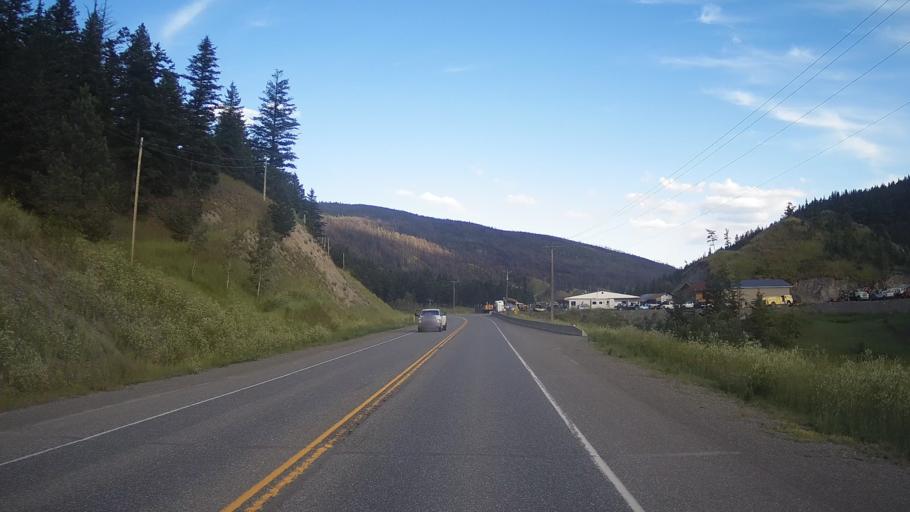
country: CA
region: British Columbia
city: Cache Creek
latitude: 51.0604
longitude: -121.5609
